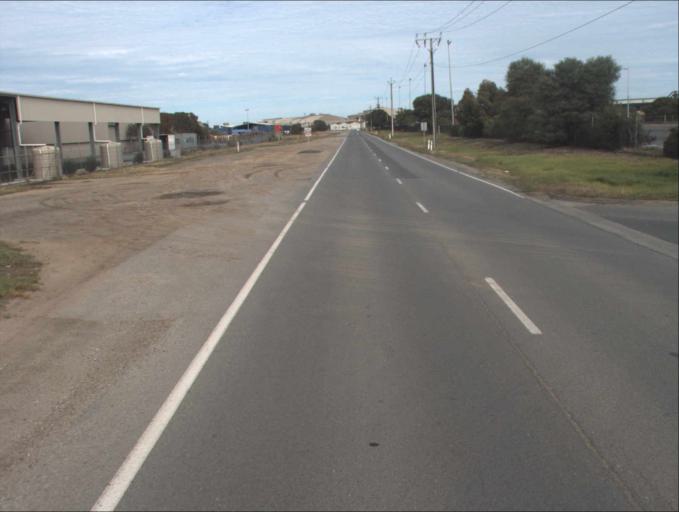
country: AU
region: South Australia
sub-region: Port Adelaide Enfield
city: Birkenhead
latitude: -34.8284
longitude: 138.5189
